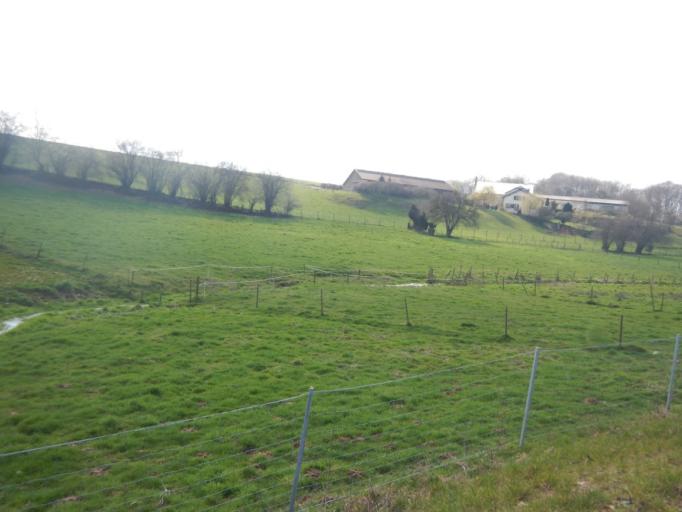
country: LU
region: Grevenmacher
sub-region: Canton d'Echternach
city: Waldbillig
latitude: 49.8110
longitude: 6.2576
